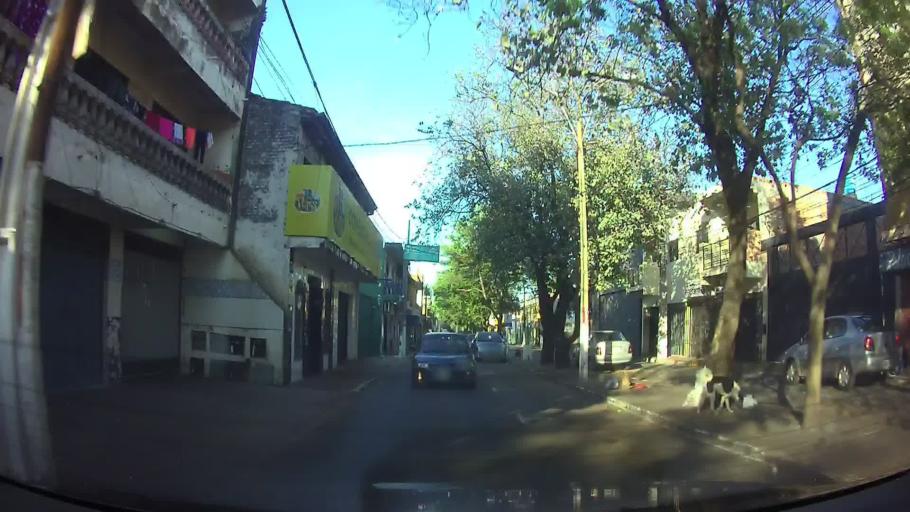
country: PY
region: Central
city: San Lorenzo
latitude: -25.3443
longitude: -57.5123
